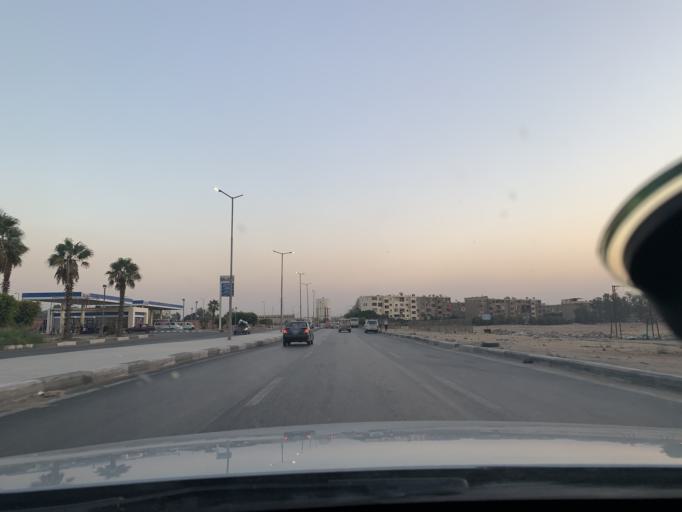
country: EG
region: Muhafazat al Qalyubiyah
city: Al Khankah
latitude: 30.1727
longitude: 31.4263
